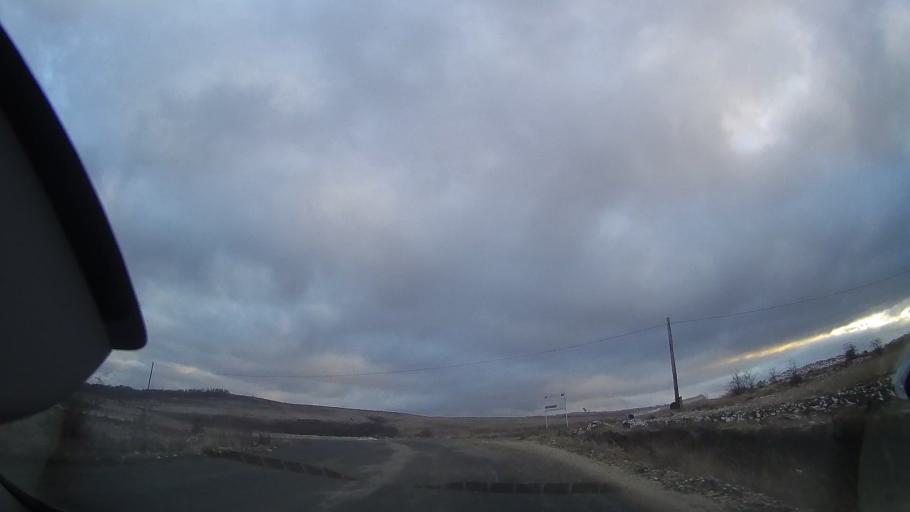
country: RO
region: Cluj
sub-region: Comuna Manastireni
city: Manastireni
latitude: 46.7782
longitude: 23.0563
